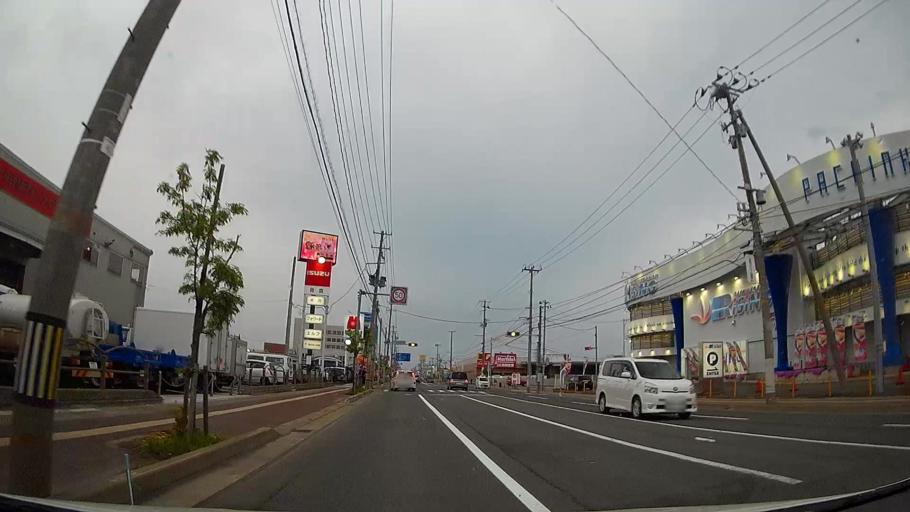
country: JP
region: Aomori
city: Aomori Shi
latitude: 40.7967
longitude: 140.7584
